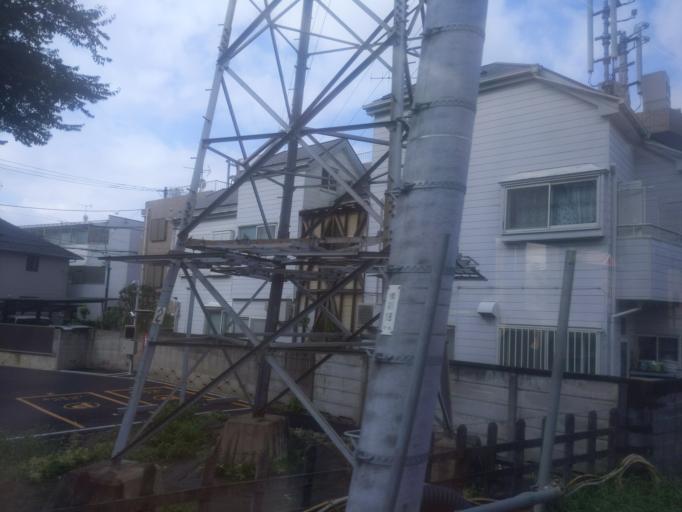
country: JP
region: Tokyo
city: Tokyo
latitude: 35.7195
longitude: 139.6626
